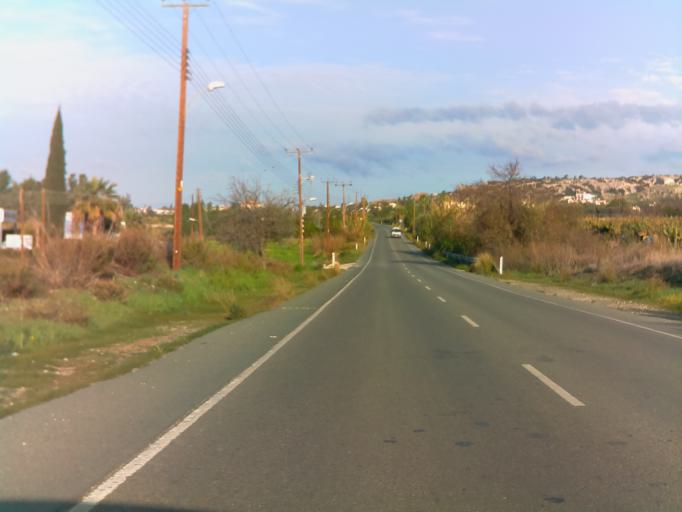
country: CY
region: Pafos
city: Pegeia
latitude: 34.8661
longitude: 32.3677
